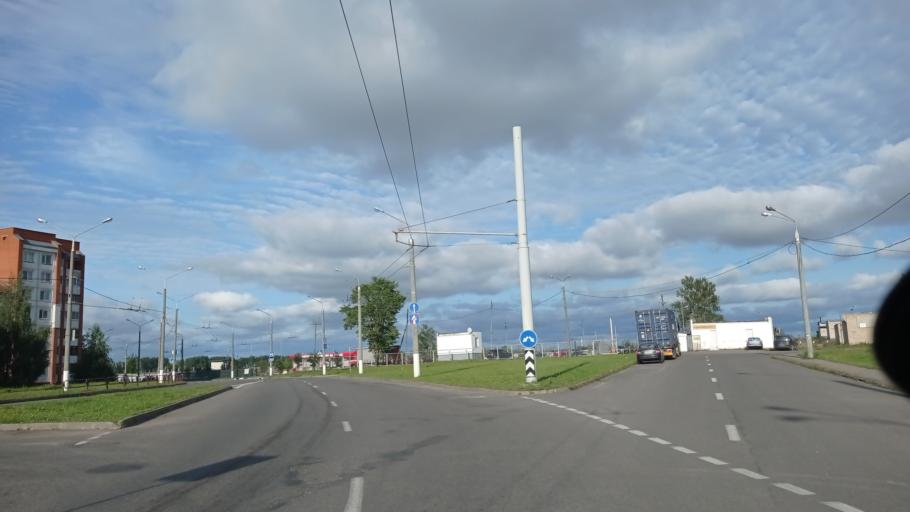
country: BY
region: Vitebsk
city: Vitebsk
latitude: 55.1972
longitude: 30.2668
